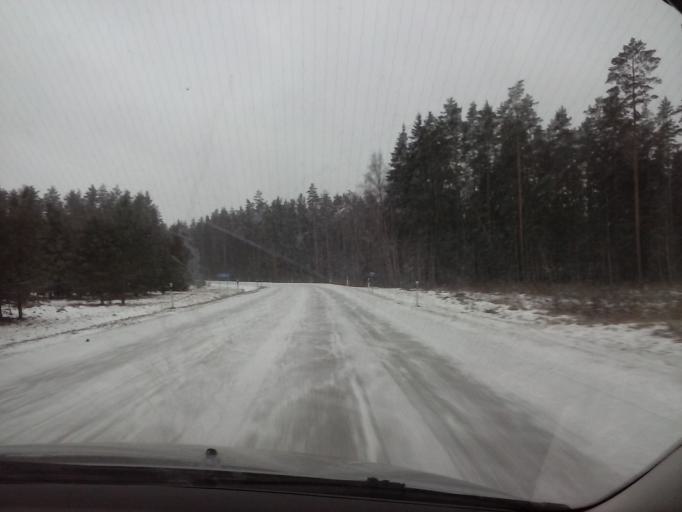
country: EE
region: Valgamaa
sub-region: Torva linn
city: Torva
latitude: 57.9930
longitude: 26.1710
